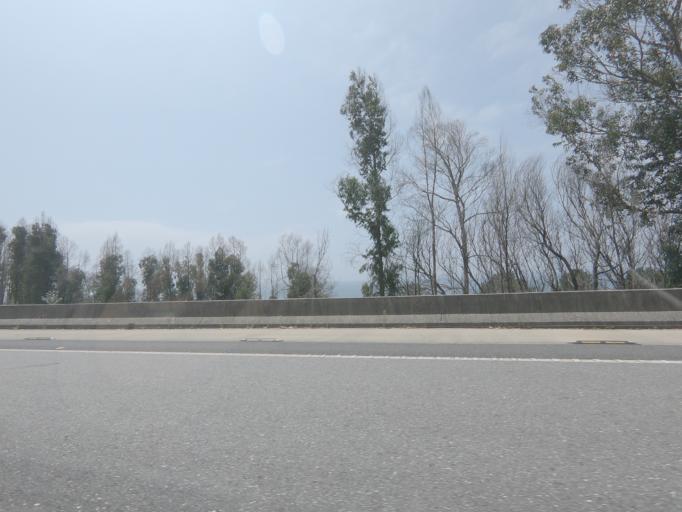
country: ES
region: Galicia
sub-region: Provincia de Pontevedra
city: A Guarda
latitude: 41.9222
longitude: -8.8804
